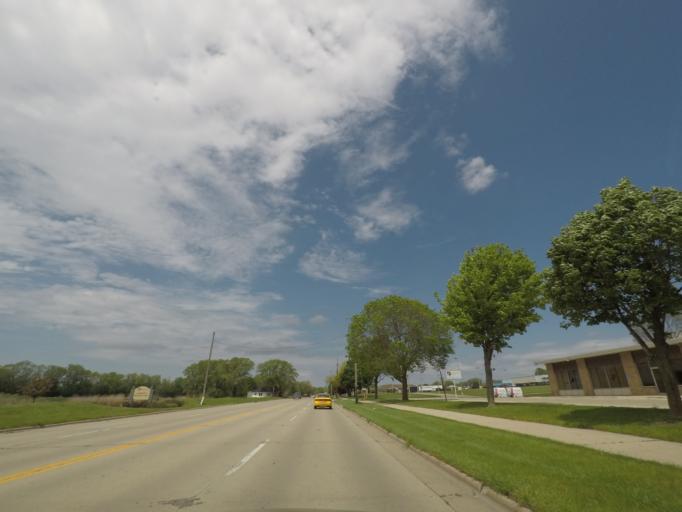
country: US
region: Wisconsin
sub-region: Rock County
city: Beloit
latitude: 42.5199
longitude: -89.0674
